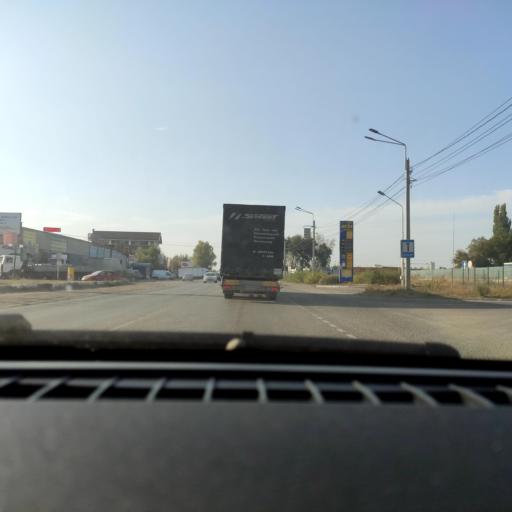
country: RU
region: Voronezj
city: Maslovka
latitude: 51.6435
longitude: 39.2958
